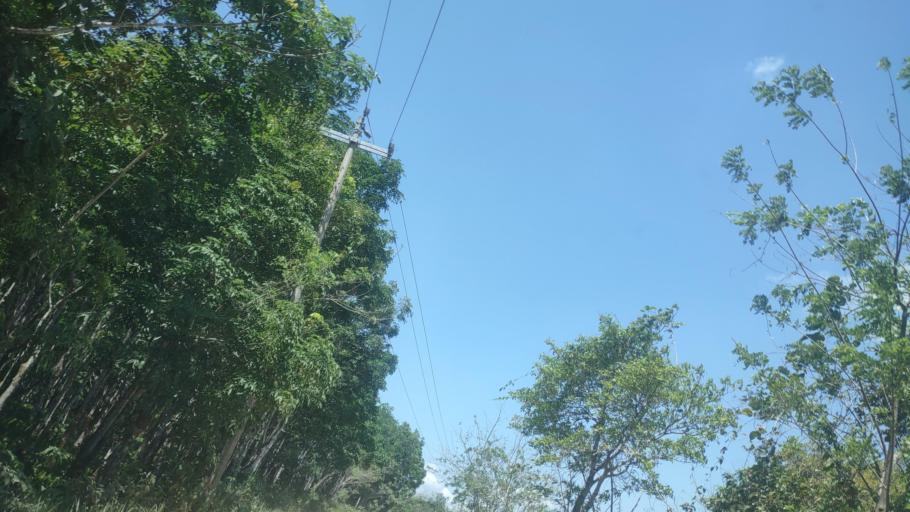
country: MX
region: Veracruz
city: Las Choapas
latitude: 17.7873
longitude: -94.1567
